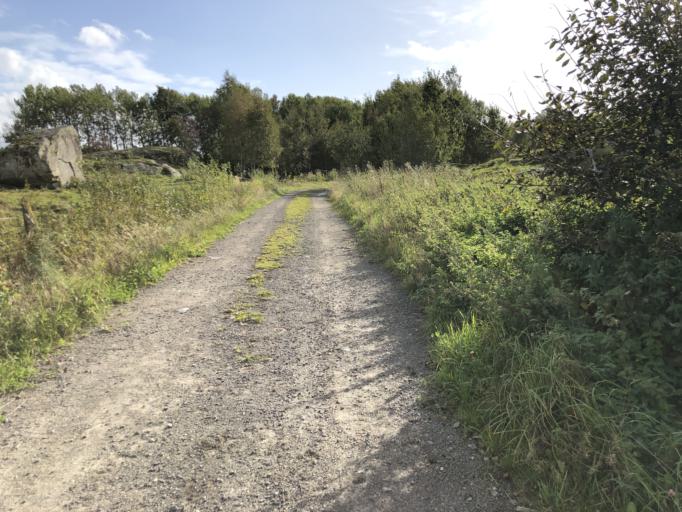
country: SE
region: Vaestra Goetaland
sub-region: Goteborg
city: Majorna
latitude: 57.7594
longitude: 11.8692
